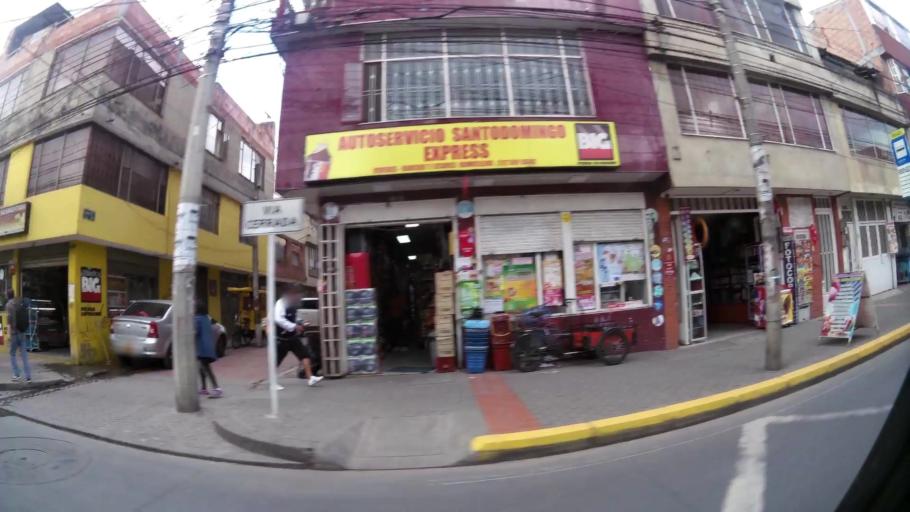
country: CO
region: Cundinamarca
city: Cota
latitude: 4.7299
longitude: -74.0986
